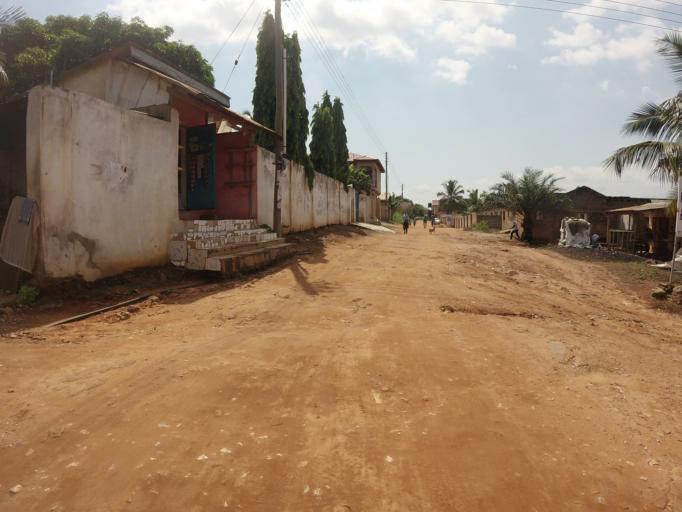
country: GH
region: Greater Accra
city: Gbawe
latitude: 5.6233
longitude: -0.3092
